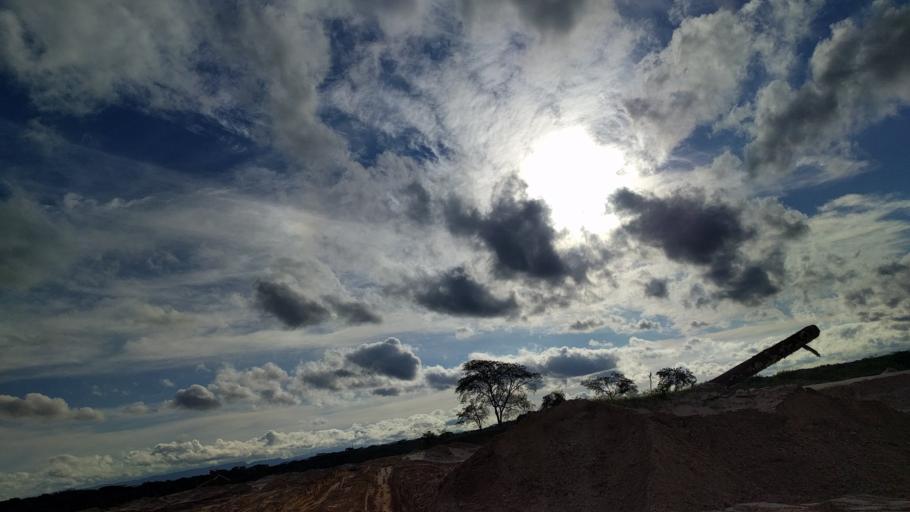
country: BO
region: Santa Cruz
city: Santa Cruz de la Sierra
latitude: -17.8531
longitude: -63.2816
